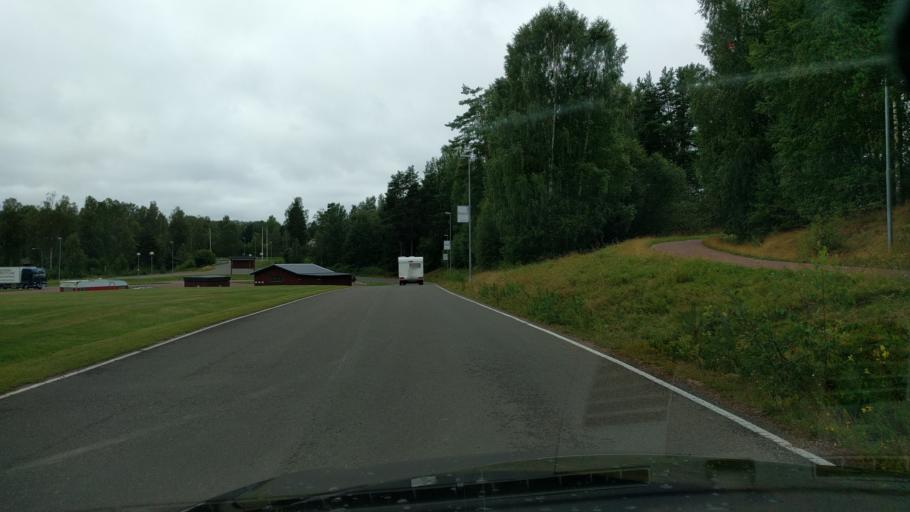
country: SE
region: Dalarna
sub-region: Mora Kommun
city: Mora
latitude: 61.0092
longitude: 14.5201
